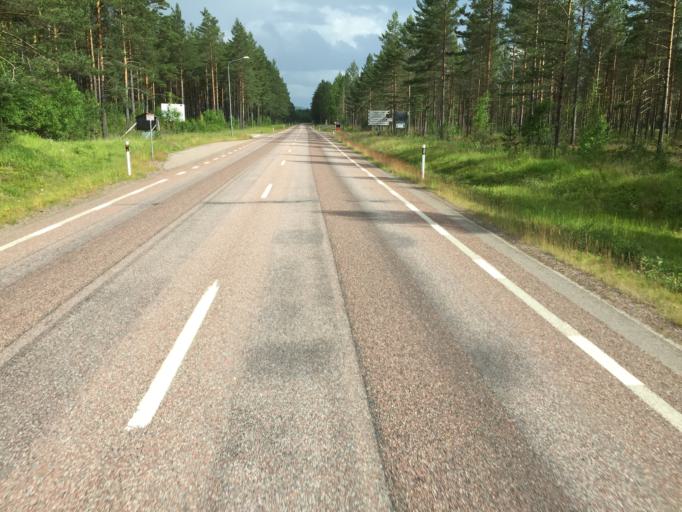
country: SE
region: Dalarna
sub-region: Vansbro Kommun
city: Jarna
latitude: 60.5361
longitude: 14.4267
